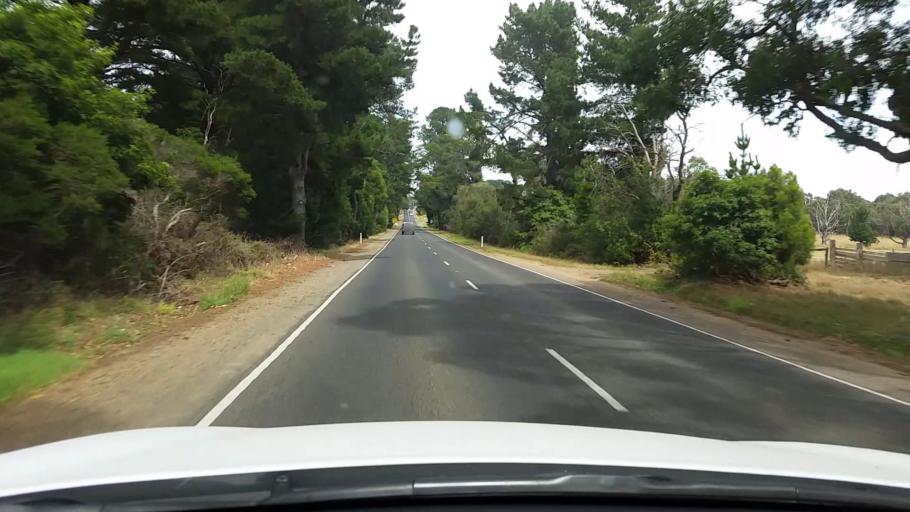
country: AU
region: Victoria
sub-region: Mornington Peninsula
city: Merricks
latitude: -38.3880
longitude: 145.0946
